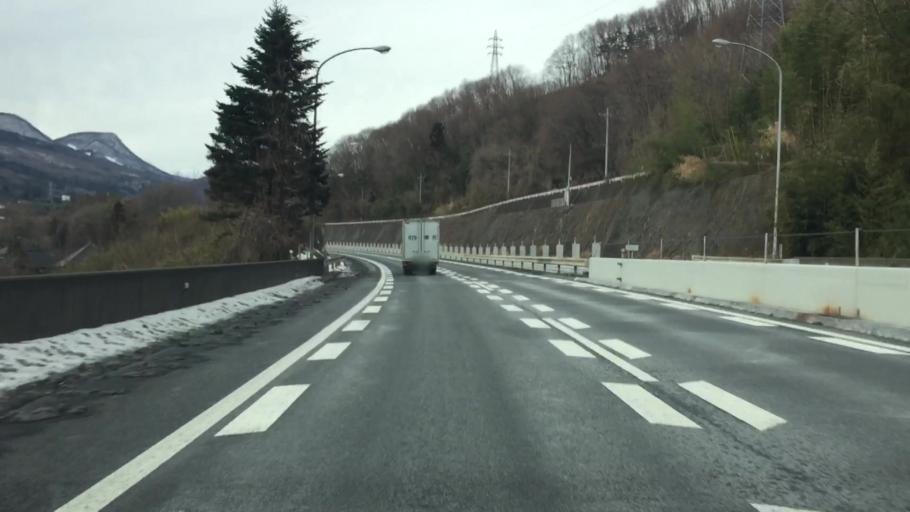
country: JP
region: Gunma
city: Numata
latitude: 36.6969
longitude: 138.9916
